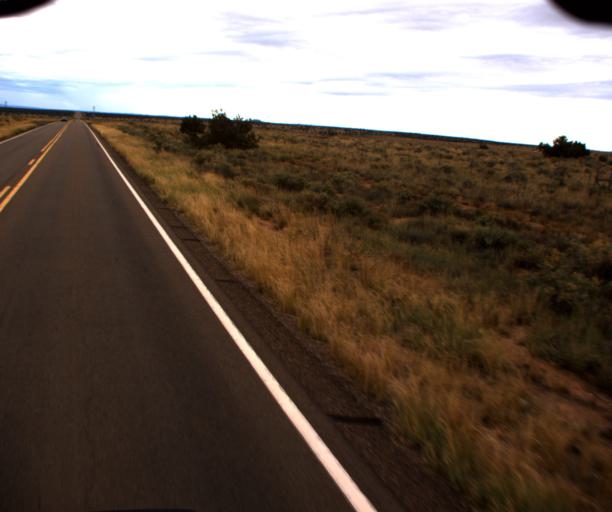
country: US
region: Arizona
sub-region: Navajo County
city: Snowflake
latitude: 34.6677
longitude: -110.1014
